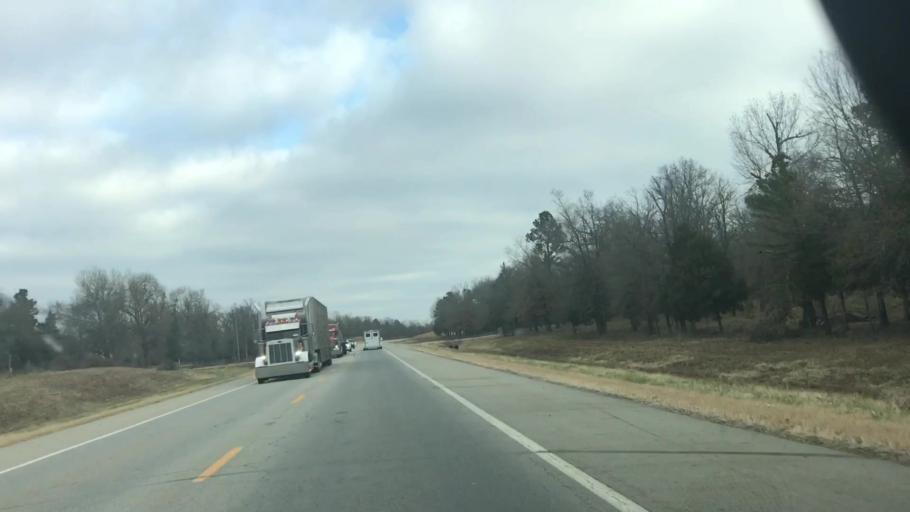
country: US
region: Arkansas
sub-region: Scott County
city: Waldron
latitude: 34.9180
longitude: -94.1071
